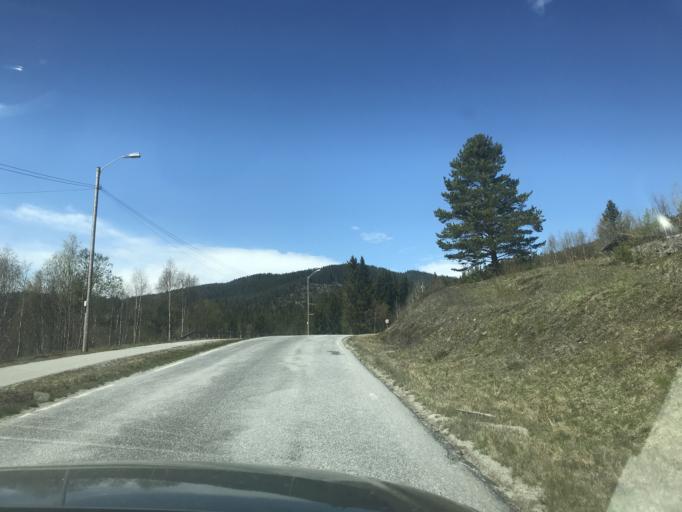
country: NO
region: Telemark
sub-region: Hjartdal
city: Sauland
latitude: 59.7560
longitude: 8.7882
